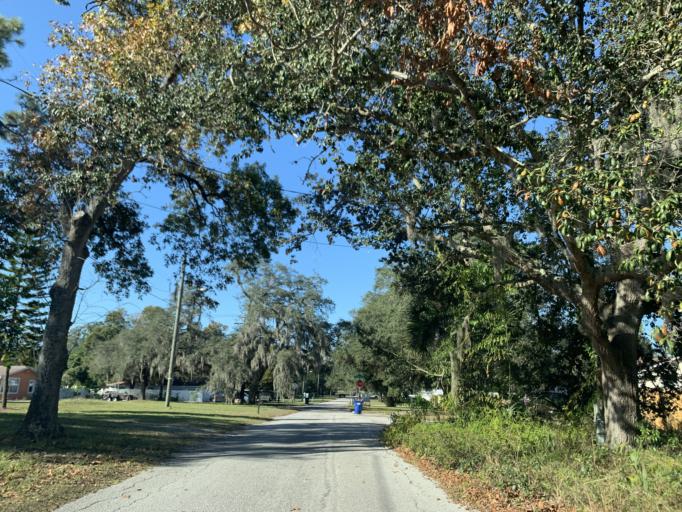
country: US
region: Florida
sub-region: Hillsborough County
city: Temple Terrace
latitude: 28.0235
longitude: -82.4128
